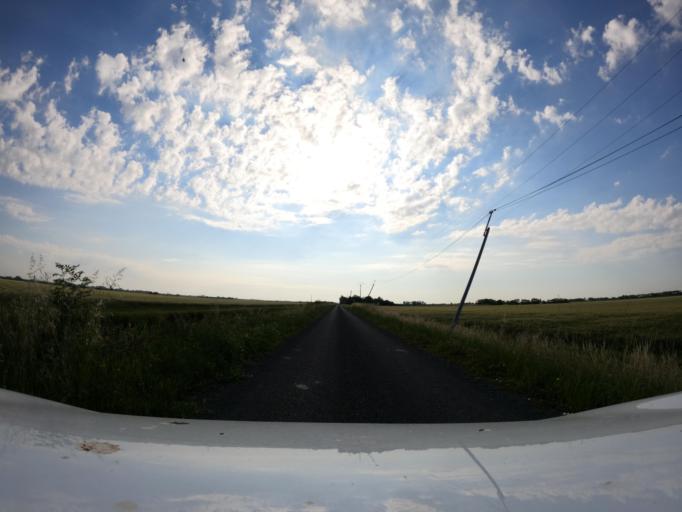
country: FR
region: Pays de la Loire
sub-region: Departement de la Vendee
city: Champagne-les-Marais
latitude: 46.3550
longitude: -1.0832
